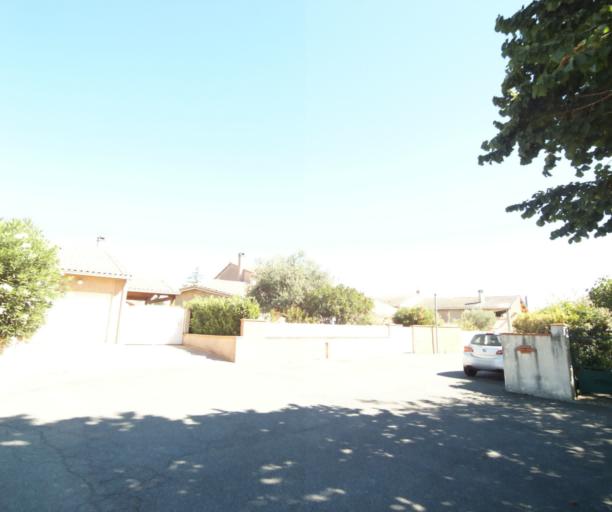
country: FR
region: Midi-Pyrenees
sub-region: Departement de la Haute-Garonne
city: Castanet-Tolosan
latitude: 43.5224
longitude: 1.4995
